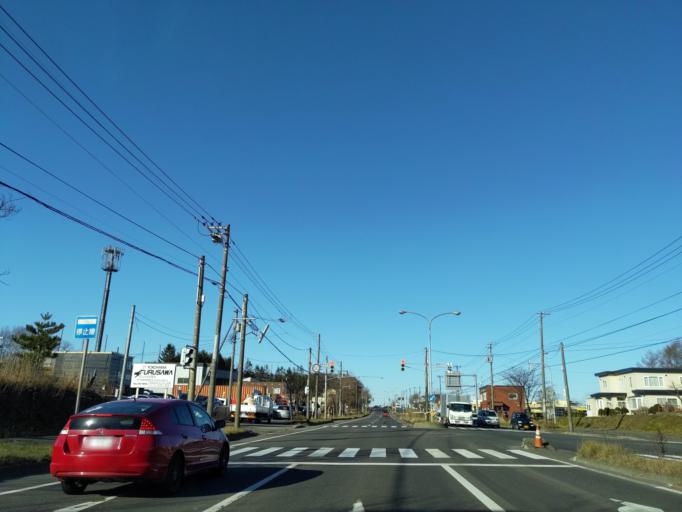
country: JP
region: Hokkaido
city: Kitahiroshima
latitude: 42.9431
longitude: 141.5029
